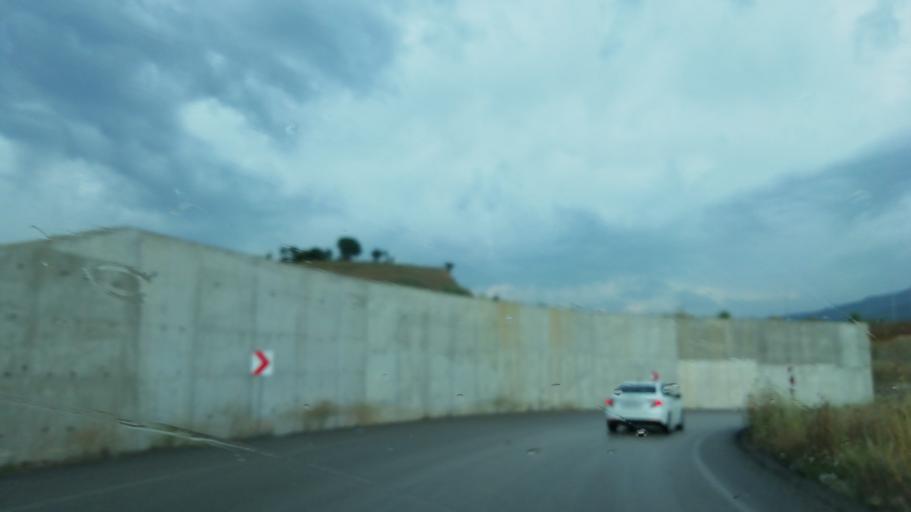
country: TR
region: Karabuk
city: Safranbolu
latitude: 41.2246
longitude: 32.7235
